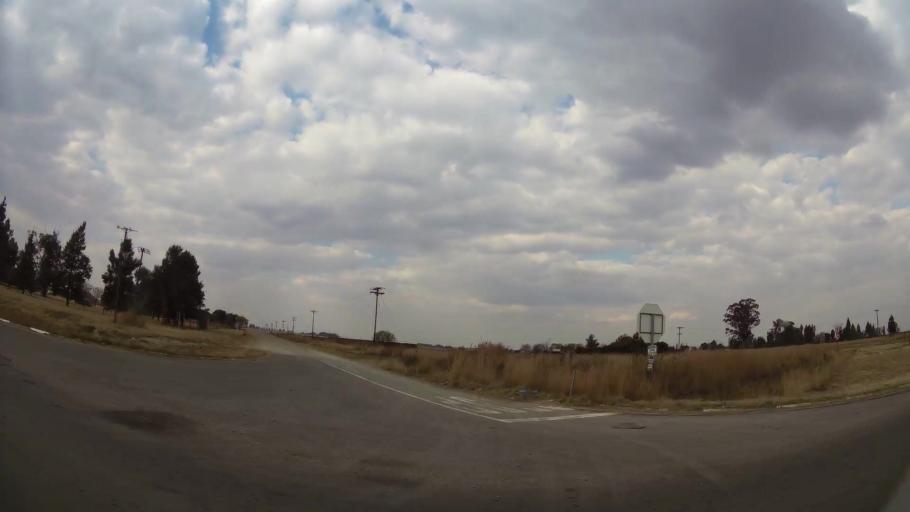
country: ZA
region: Mpumalanga
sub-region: Nkangala District Municipality
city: Delmas
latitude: -26.2985
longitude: 28.6069
